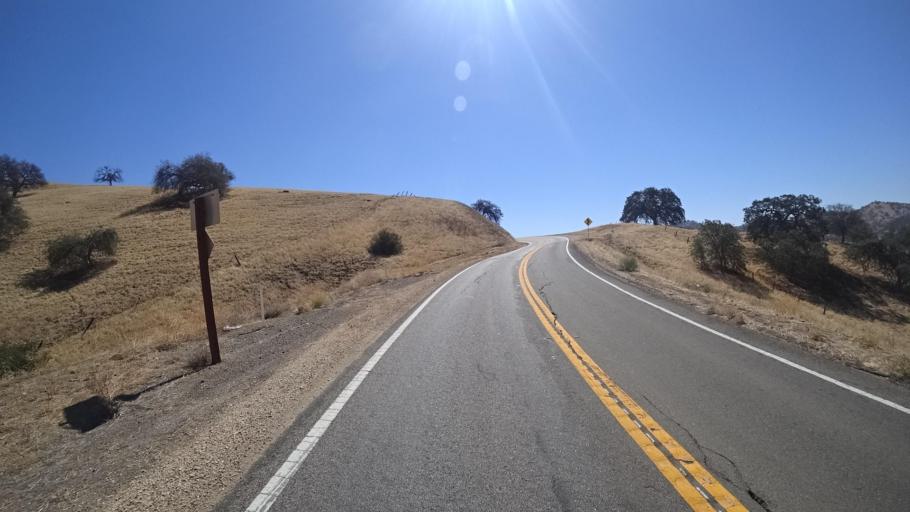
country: US
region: California
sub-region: Monterey County
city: King City
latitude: 36.1916
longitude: -120.8032
